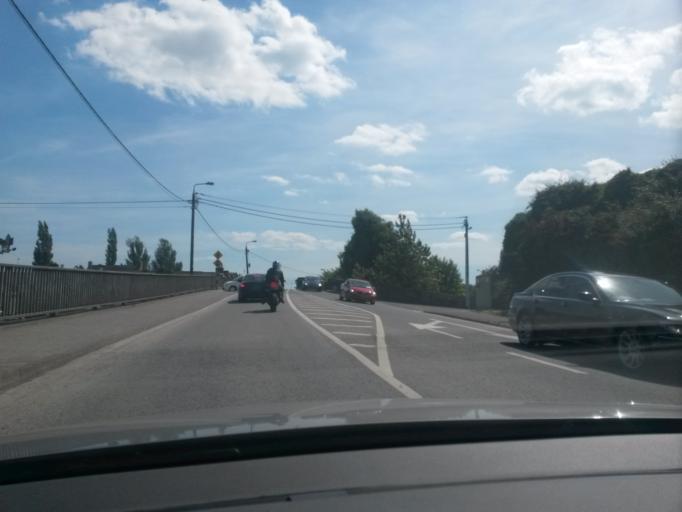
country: IE
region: Leinster
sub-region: Kildare
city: Sallins
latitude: 53.2498
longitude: -6.6653
